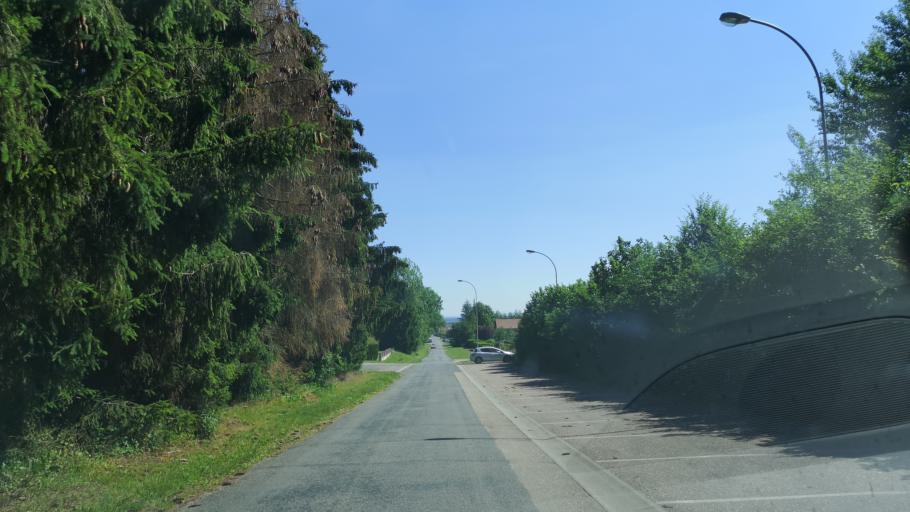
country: FR
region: Lorraine
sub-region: Departement de la Meuse
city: Vigneulles-les-Hattonchatel
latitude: 49.0338
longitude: 5.6513
